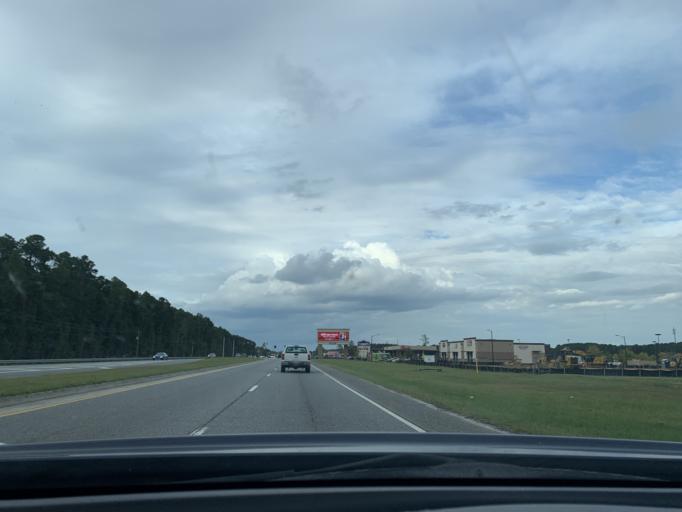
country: US
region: Georgia
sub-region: Chatham County
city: Pooler
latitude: 32.0911
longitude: -81.2755
